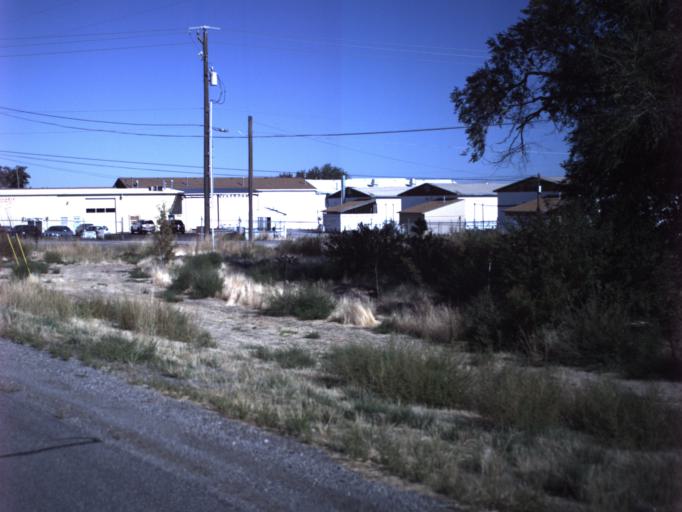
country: US
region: Utah
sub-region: Tooele County
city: Grantsville
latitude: 40.6018
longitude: -112.4841
